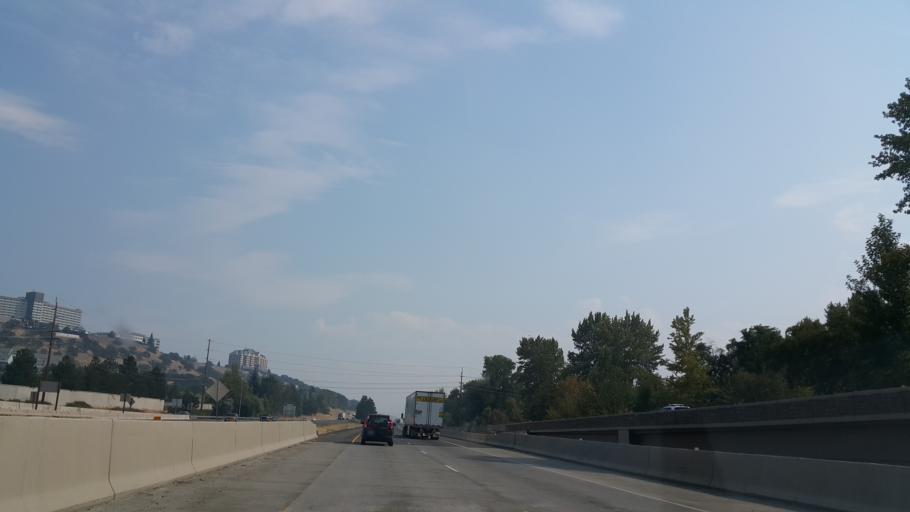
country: US
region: Oregon
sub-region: Jackson County
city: Medford
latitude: 42.3107
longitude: -122.8484
